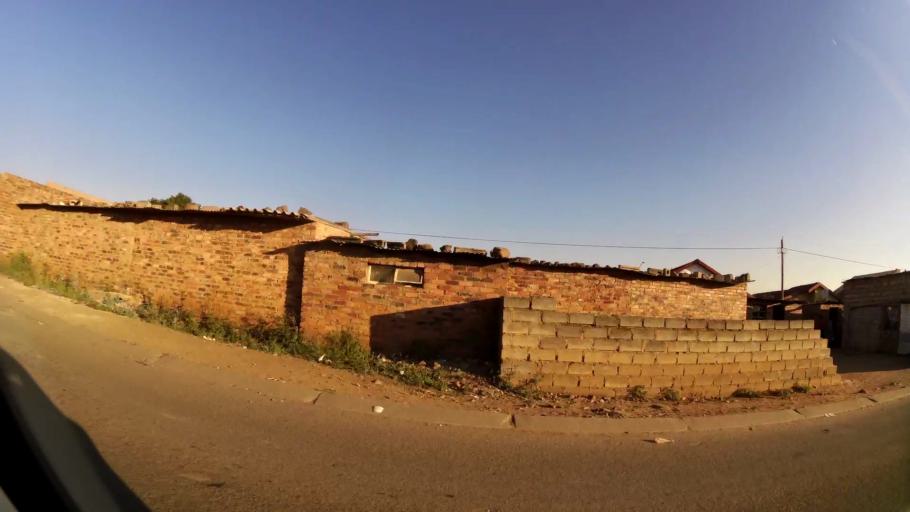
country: ZA
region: Gauteng
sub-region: City of Tshwane Metropolitan Municipality
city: Cullinan
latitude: -25.7236
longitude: 28.3819
